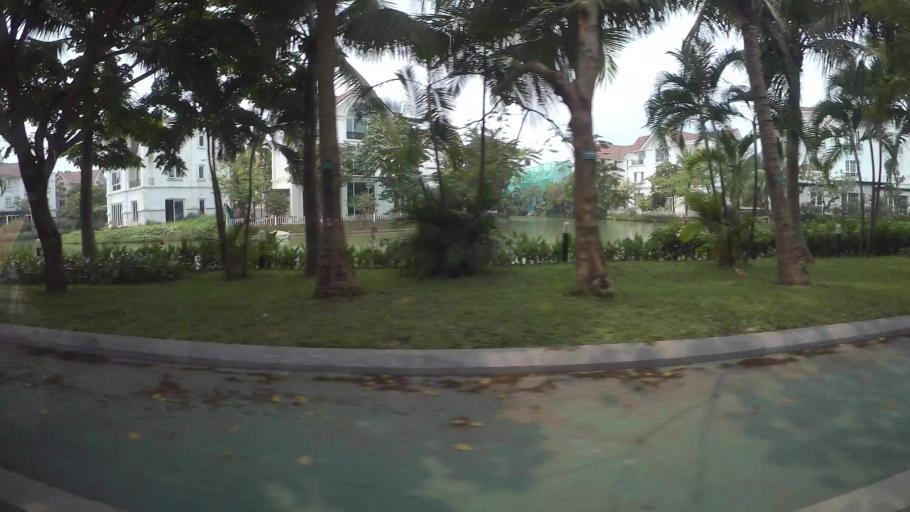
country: VN
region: Ha Noi
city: Trau Quy
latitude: 21.0524
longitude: 105.9140
